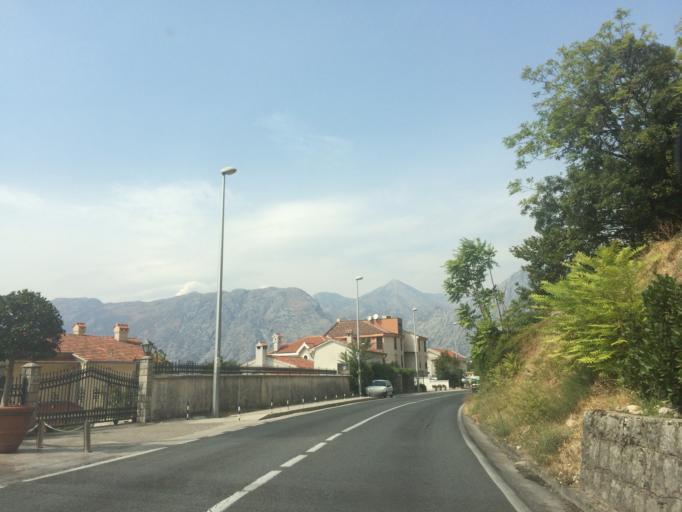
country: ME
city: Dobrota
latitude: 42.4600
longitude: 18.7653
